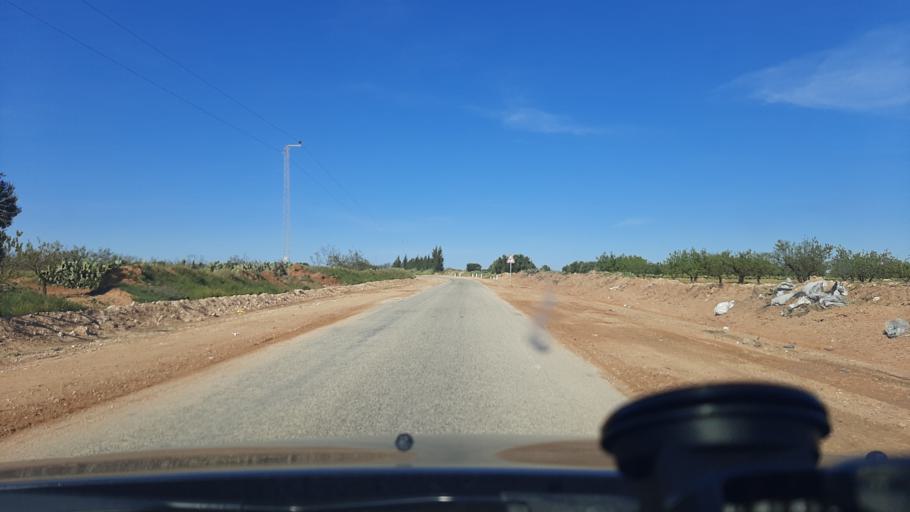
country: TN
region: Safaqis
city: Sfax
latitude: 34.9123
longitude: 10.5881
